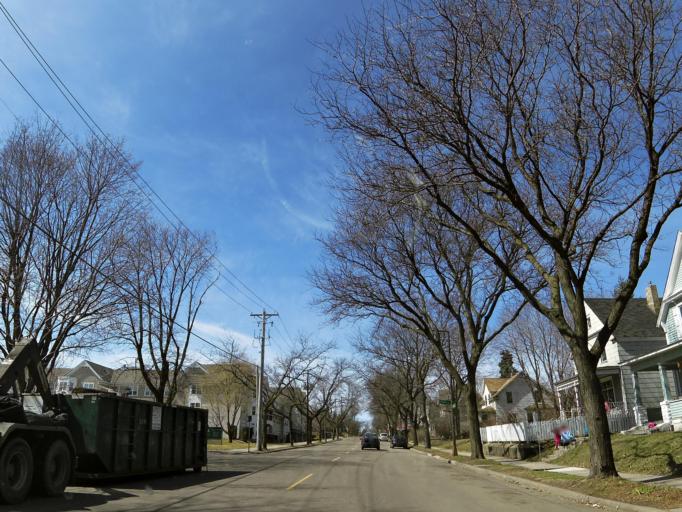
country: US
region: Minnesota
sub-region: Ramsey County
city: Saint Paul
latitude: 44.9488
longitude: -93.0534
